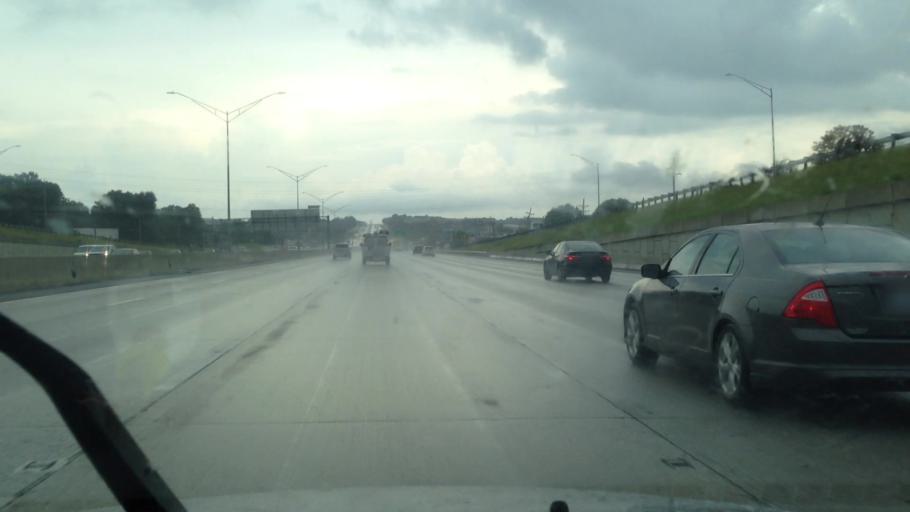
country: US
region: North Carolina
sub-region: Guilford County
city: Jamestown
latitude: 36.0756
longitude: -79.9435
